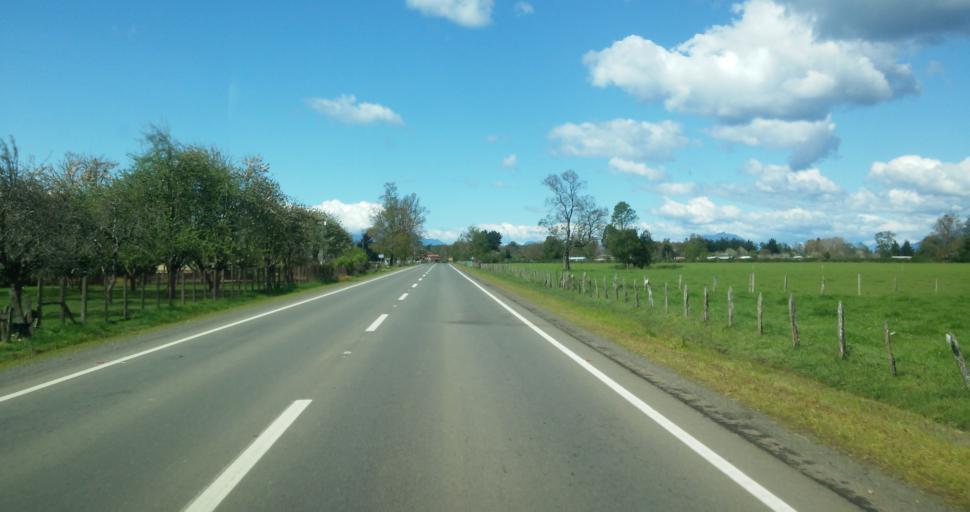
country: CL
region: Los Rios
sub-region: Provincia del Ranco
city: Rio Bueno
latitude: -40.2399
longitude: -72.6001
